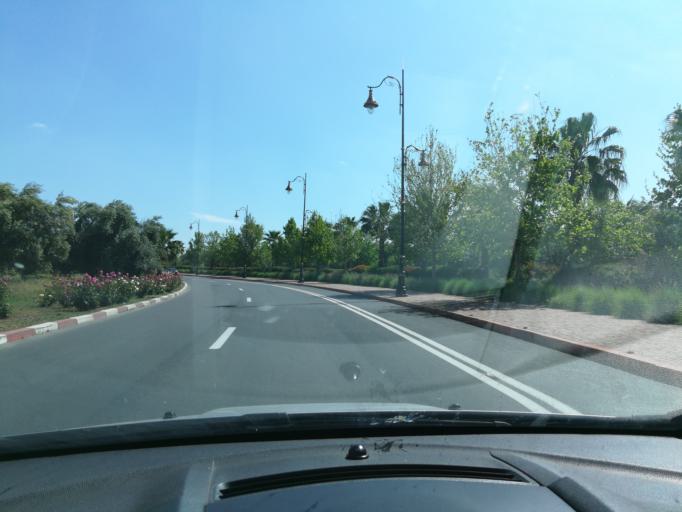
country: MA
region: Marrakech-Tensift-Al Haouz
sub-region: Marrakech
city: Marrakesh
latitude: 31.6150
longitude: -8.0071
